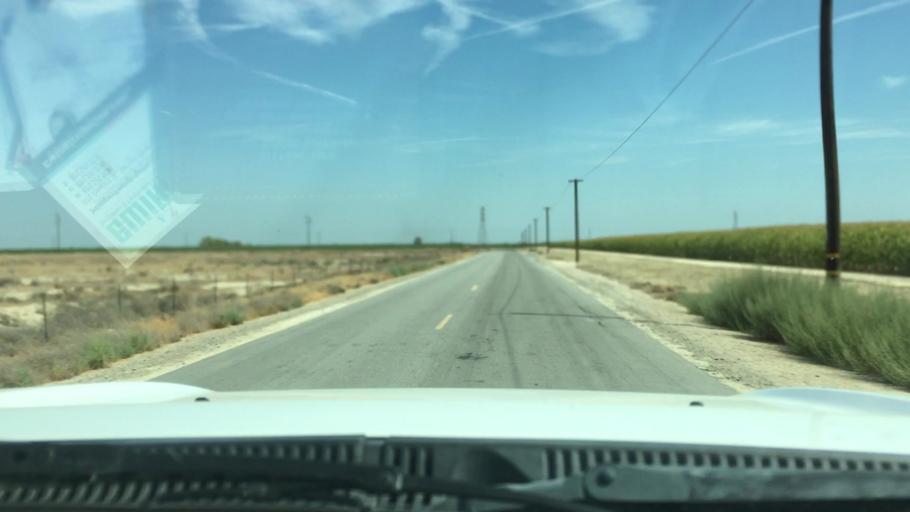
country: US
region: California
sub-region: Kern County
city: Buttonwillow
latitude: 35.4371
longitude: -119.3761
